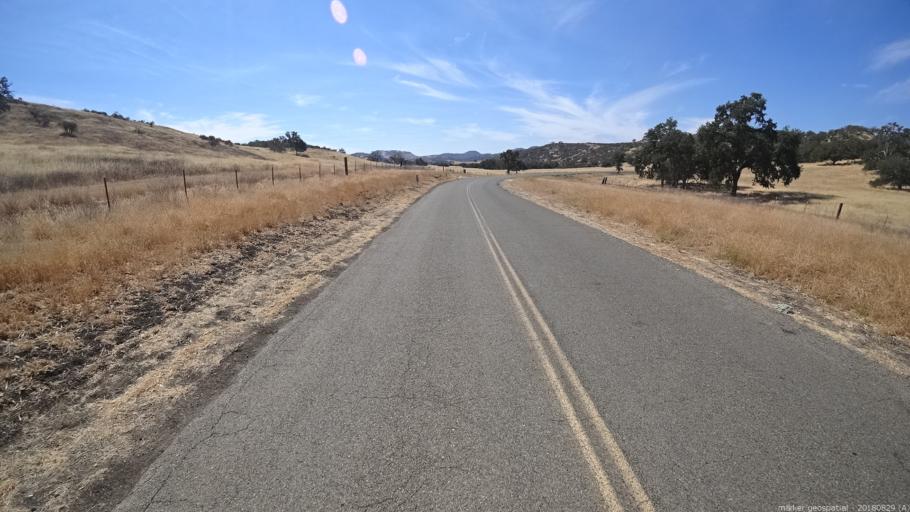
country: US
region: California
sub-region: San Luis Obispo County
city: Lake Nacimiento
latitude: 35.8302
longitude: -120.9761
